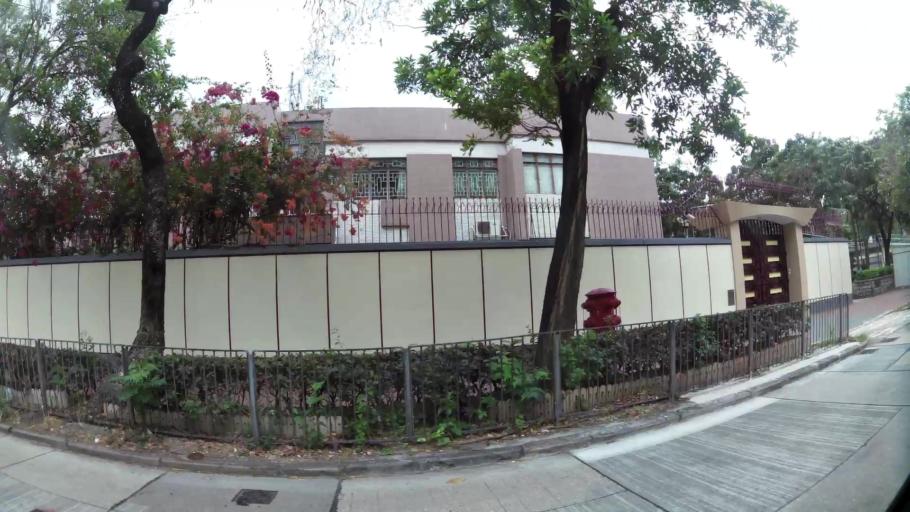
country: HK
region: Wong Tai Sin
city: Wong Tai Sin
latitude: 22.3400
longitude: 114.1788
